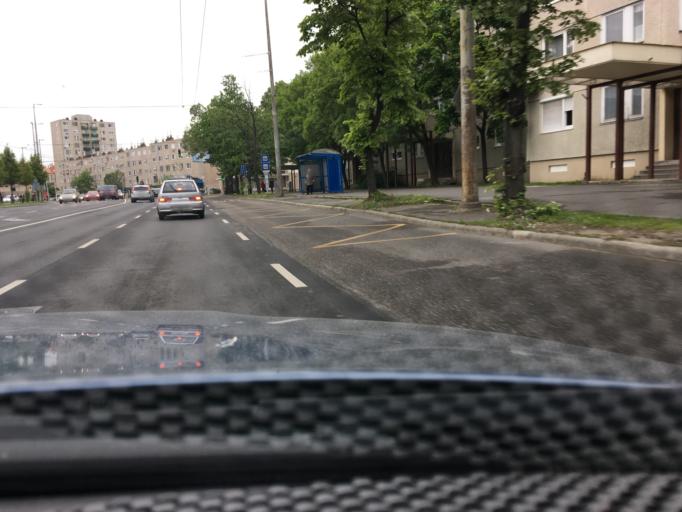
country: HU
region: Hajdu-Bihar
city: Debrecen
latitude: 47.5304
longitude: 21.6314
